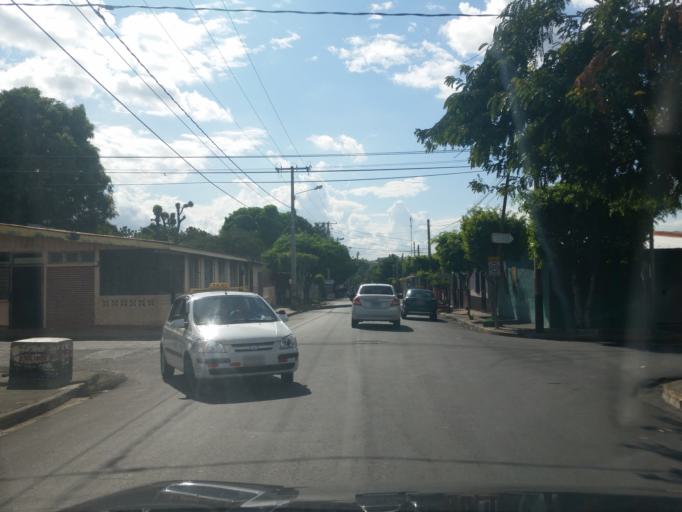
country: NI
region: Managua
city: Managua
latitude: 12.1391
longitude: -86.2569
